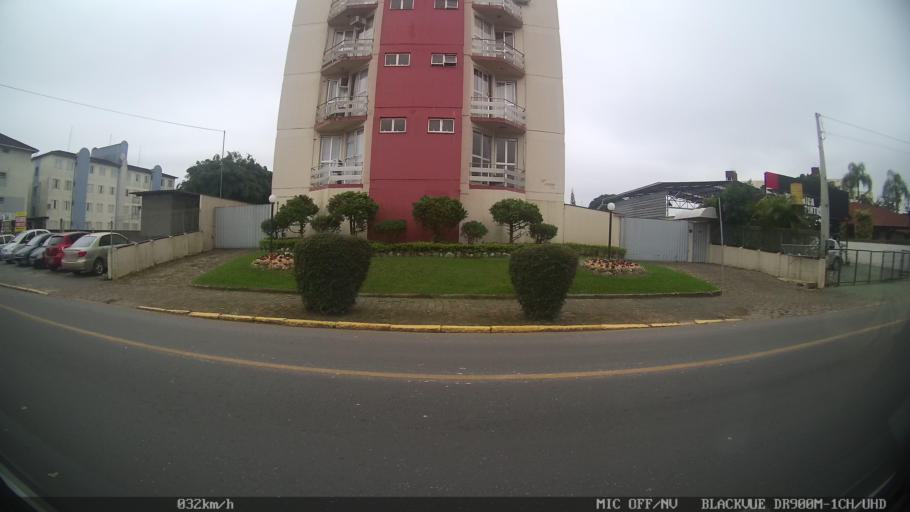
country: BR
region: Santa Catarina
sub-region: Joinville
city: Joinville
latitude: -26.2873
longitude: -48.8417
